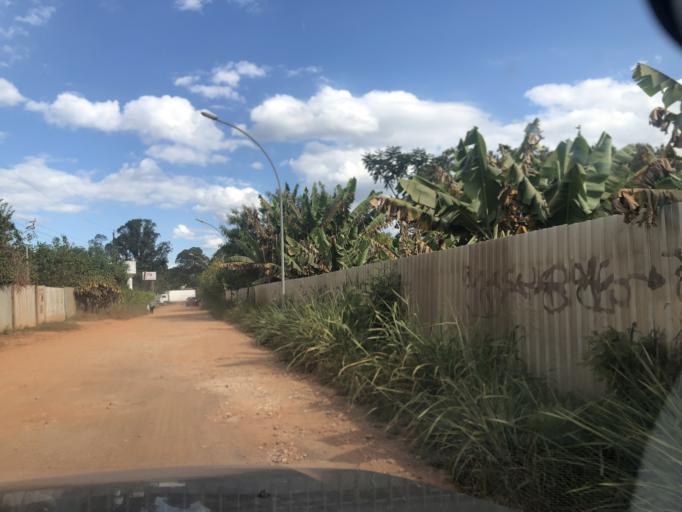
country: BR
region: Federal District
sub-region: Brasilia
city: Brasilia
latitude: -15.8747
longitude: -47.9700
